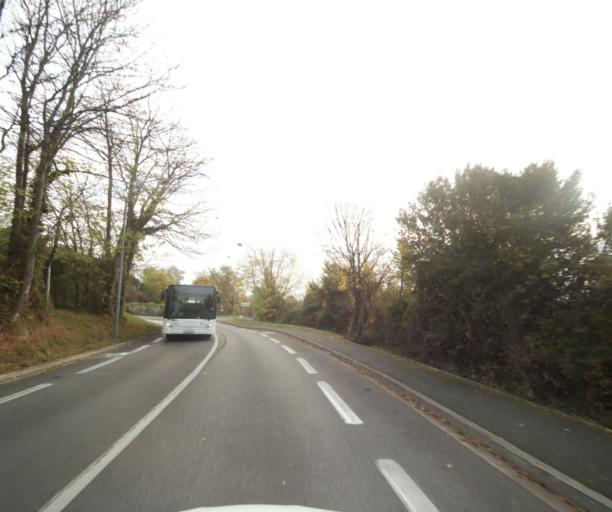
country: FR
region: Poitou-Charentes
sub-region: Departement de la Charente-Maritime
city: Saintes
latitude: 45.7485
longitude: -0.6560
